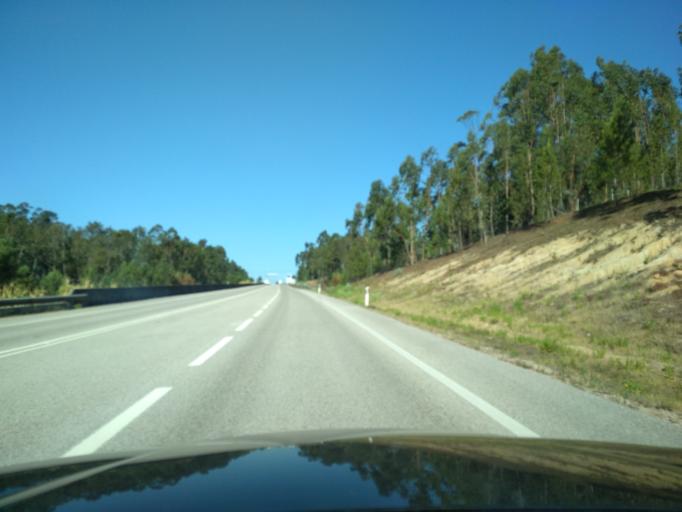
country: PT
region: Leiria
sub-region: Pombal
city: Lourical
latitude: 39.9880
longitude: -8.7712
